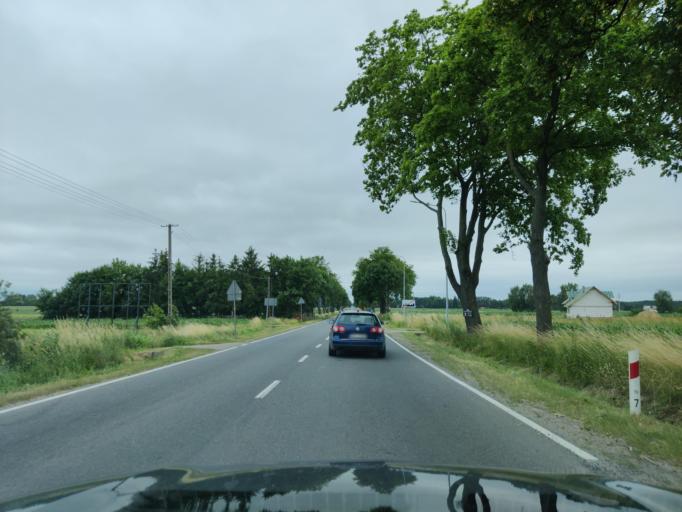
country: PL
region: Masovian Voivodeship
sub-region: Powiat ostrolecki
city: Myszyniec
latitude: 53.4312
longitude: 21.3622
